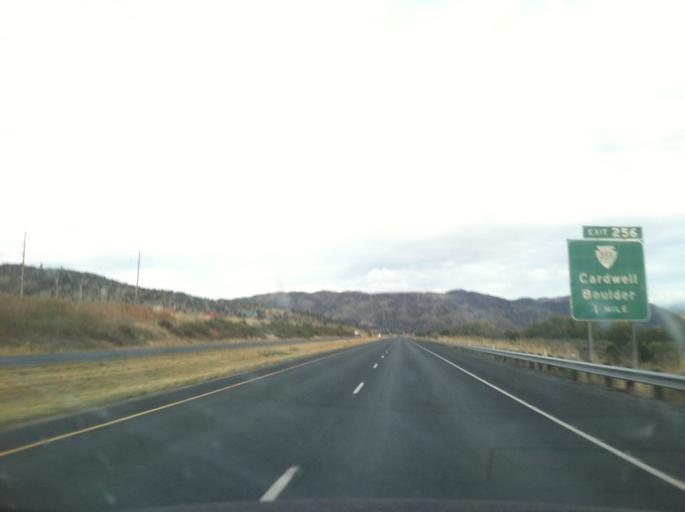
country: US
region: Montana
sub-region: Jefferson County
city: Whitehall
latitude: 45.8734
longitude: -111.9798
